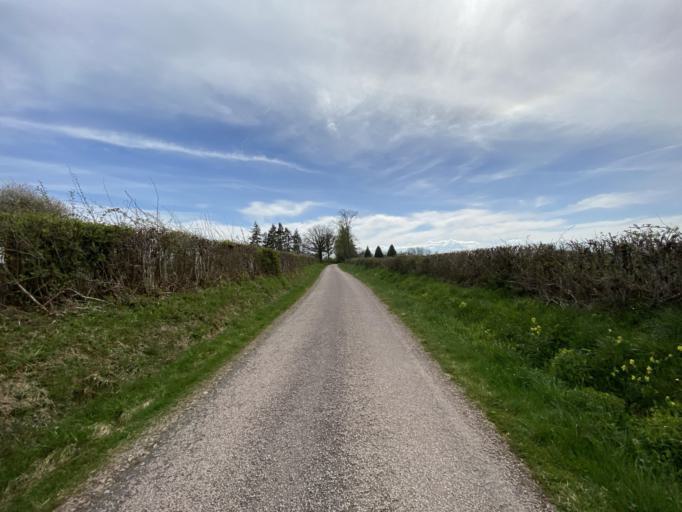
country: FR
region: Bourgogne
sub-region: Departement de la Cote-d'Or
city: Saulieu
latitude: 47.2790
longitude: 4.2126
